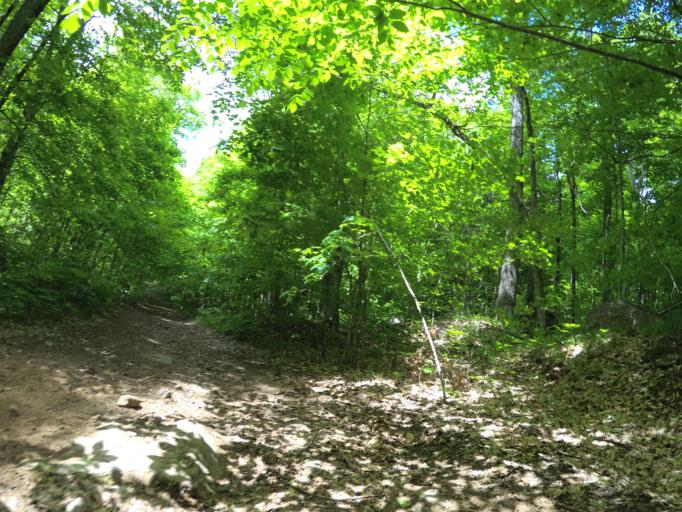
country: CA
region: Ontario
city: Renfrew
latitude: 45.0584
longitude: -76.8605
